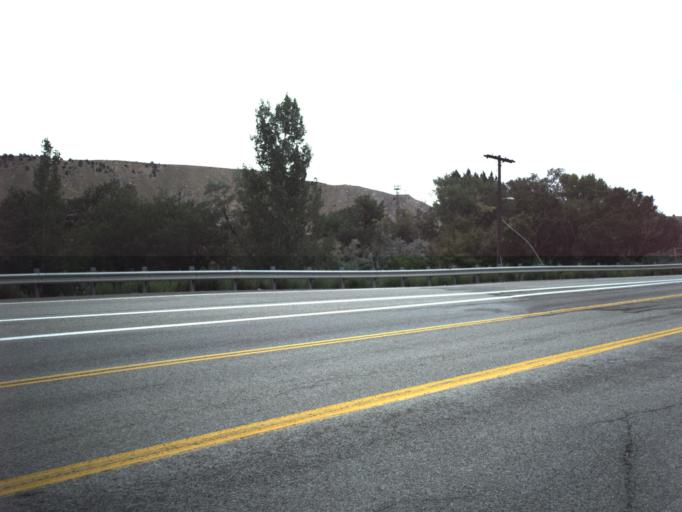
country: US
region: Utah
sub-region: Carbon County
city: Helper
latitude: 39.6890
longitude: -110.8565
